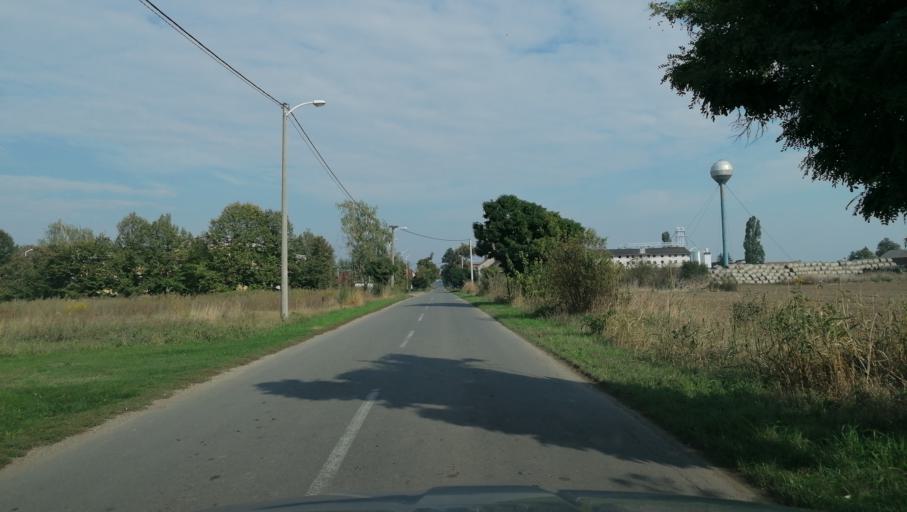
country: BA
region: Republika Srpska
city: Popovi
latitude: 44.7705
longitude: 19.2511
